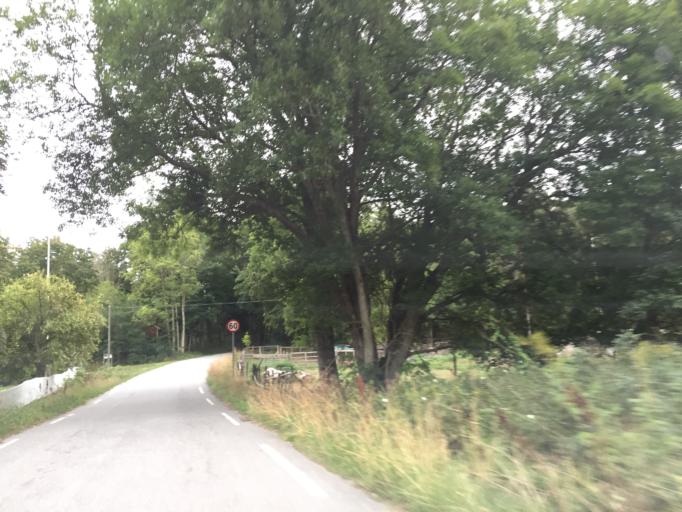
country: NO
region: Ostfold
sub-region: Hvaler
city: Skjaerhalden
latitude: 59.0755
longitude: 11.0043
